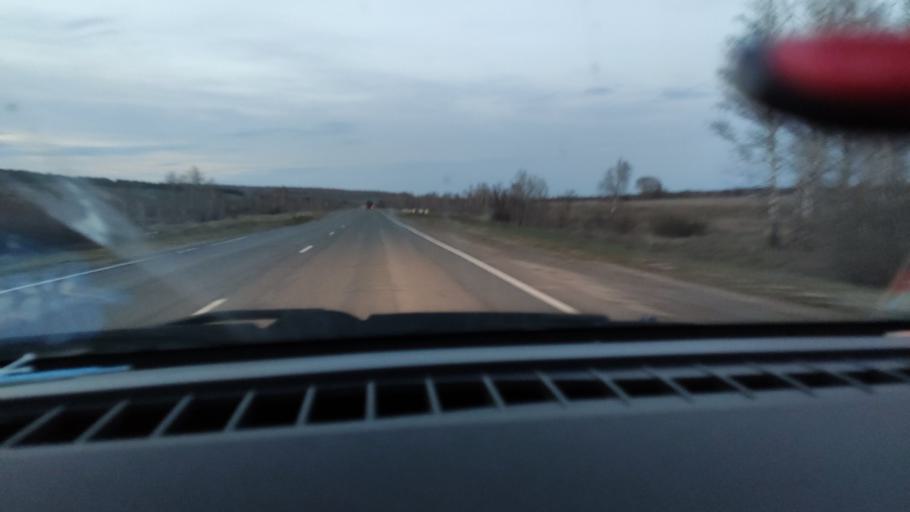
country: RU
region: Saratov
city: Sinodskoye
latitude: 52.0597
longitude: 46.7623
